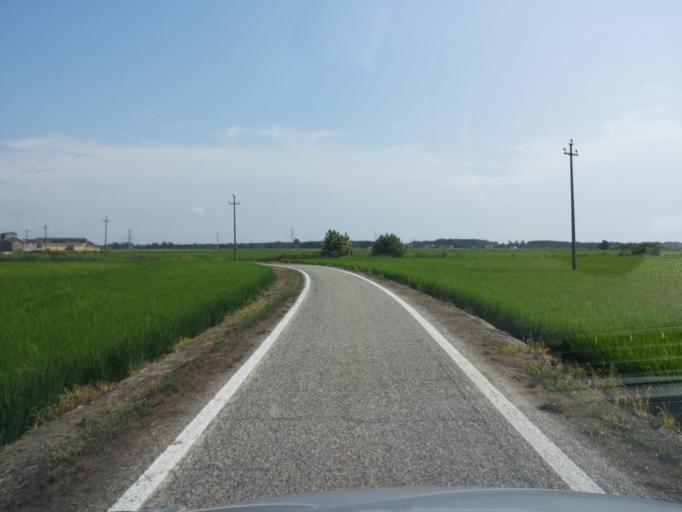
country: IT
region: Piedmont
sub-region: Provincia di Vercelli
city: Pezzana
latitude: 45.2647
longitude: 8.5201
